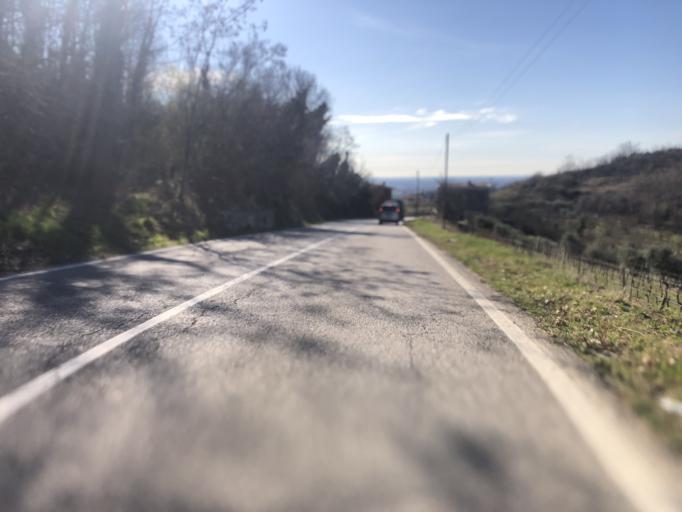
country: IT
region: Veneto
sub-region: Provincia di Verona
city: Sant'Ambrogio di Valpollicella
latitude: 45.5329
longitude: 10.8338
